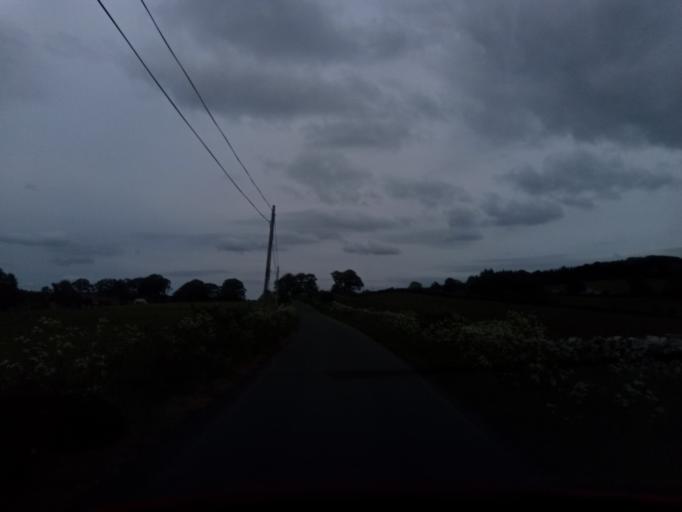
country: GB
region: Scotland
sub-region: The Scottish Borders
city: Selkirk
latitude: 55.5552
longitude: -2.8190
